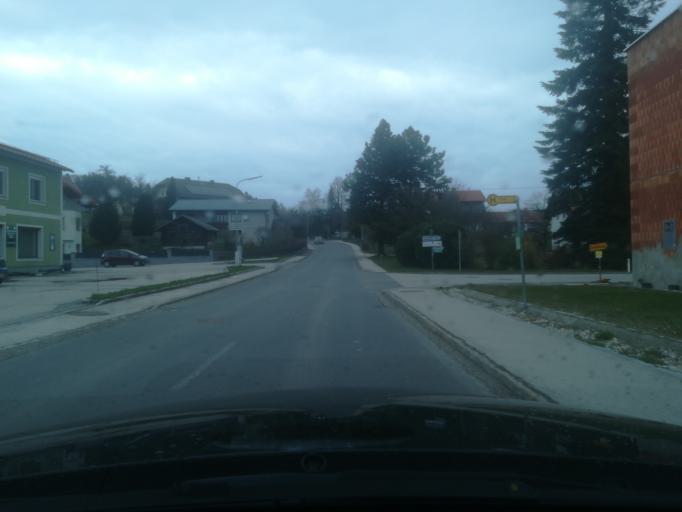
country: AT
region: Upper Austria
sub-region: Politischer Bezirk Urfahr-Umgebung
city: Feldkirchen an der Donau
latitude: 48.3389
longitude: 13.9571
